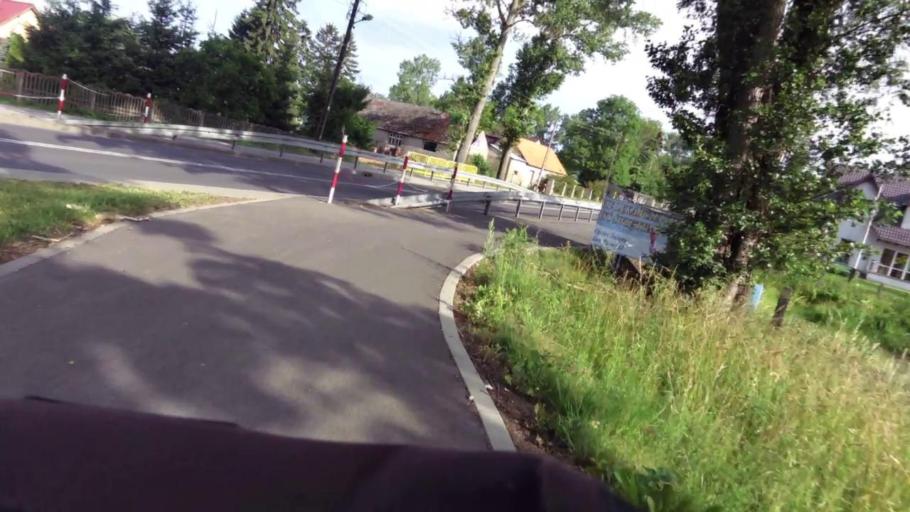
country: PL
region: West Pomeranian Voivodeship
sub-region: Powiat kamienski
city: Kamien Pomorski
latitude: 53.9976
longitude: 14.8173
